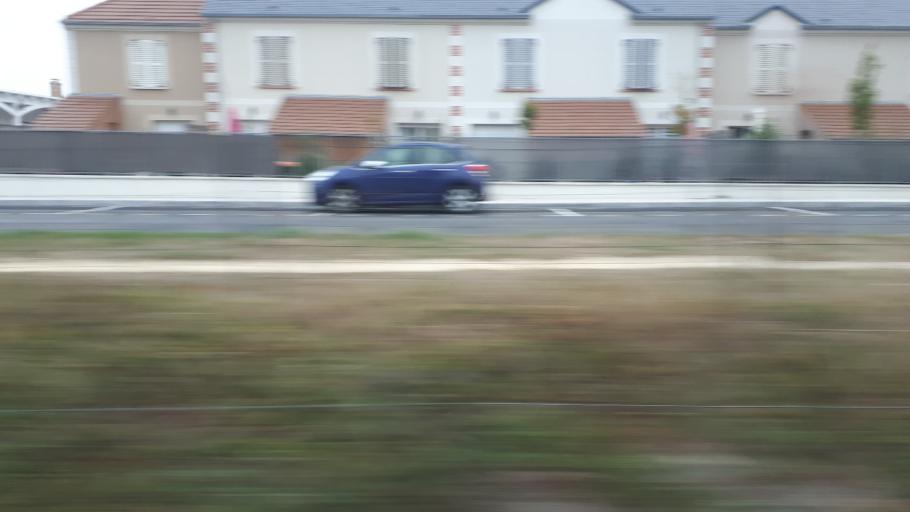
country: FR
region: Centre
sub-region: Departement d'Indre-et-Loire
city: Chanceaux-sur-Choisille
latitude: 47.4591
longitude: 0.7041
